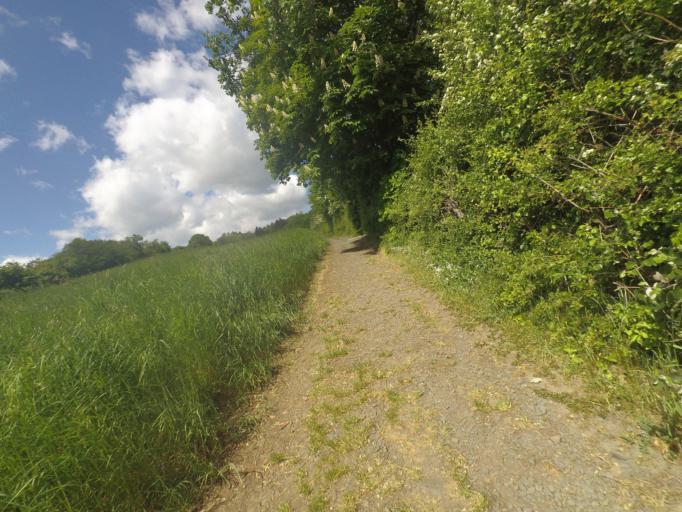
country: DE
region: Rheinland-Pfalz
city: Kirchheimbolanden
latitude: 49.6673
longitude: 8.0020
